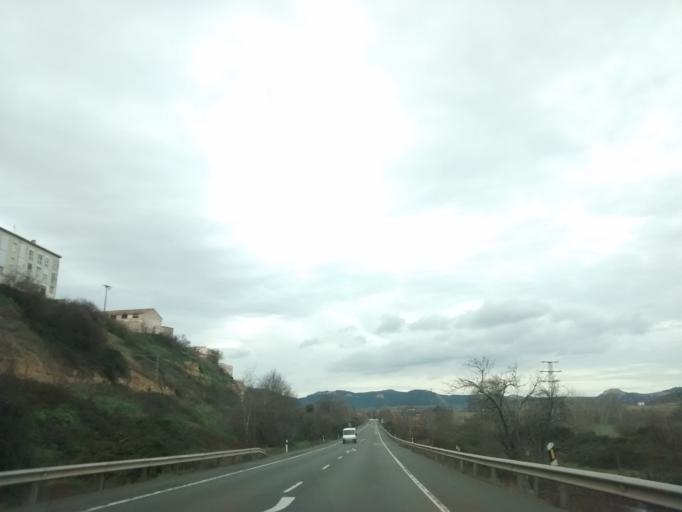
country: ES
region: La Rioja
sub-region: Provincia de La Rioja
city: Haro
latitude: 42.5748
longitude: -2.8408
